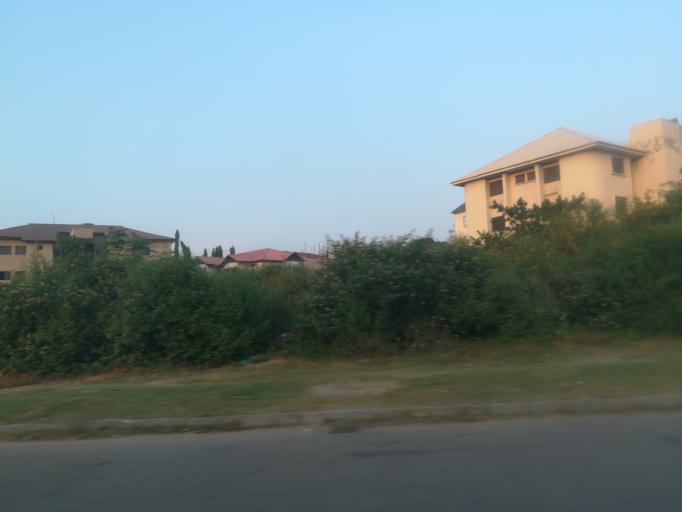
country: NG
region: Abuja Federal Capital Territory
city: Abuja
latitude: 9.0637
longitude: 7.4413
